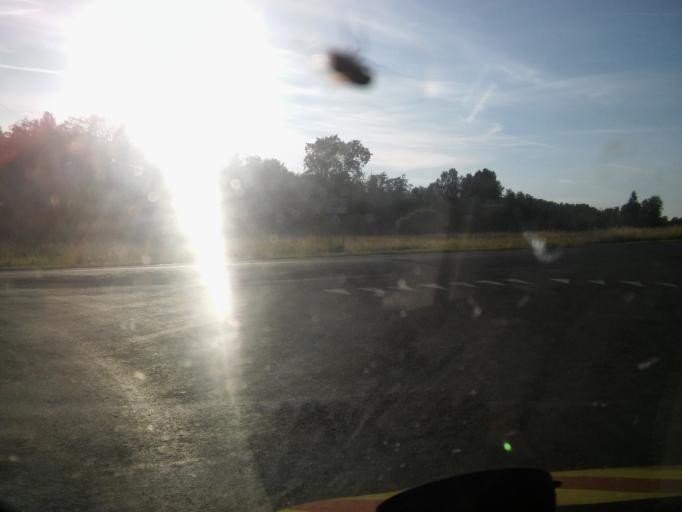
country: EE
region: Valgamaa
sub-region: Torva linn
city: Torva
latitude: 58.0213
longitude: 25.8807
